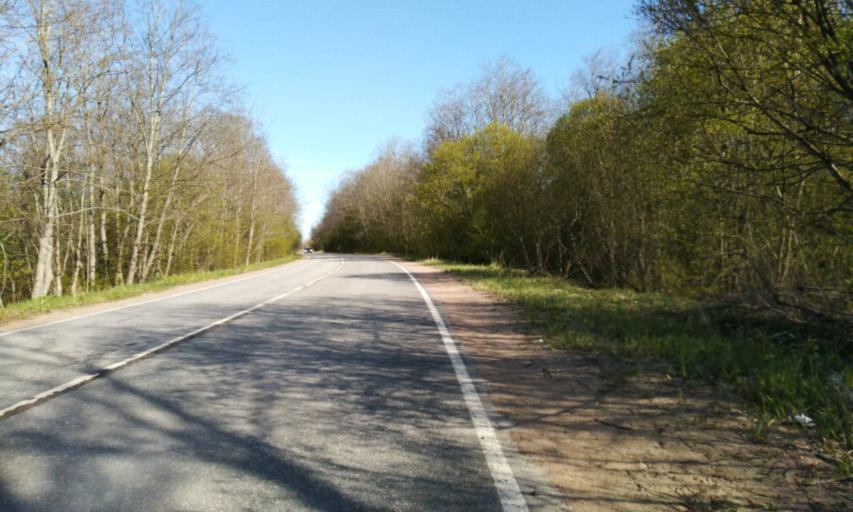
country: RU
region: Leningrad
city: Leskolovo
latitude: 60.3249
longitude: 30.4277
